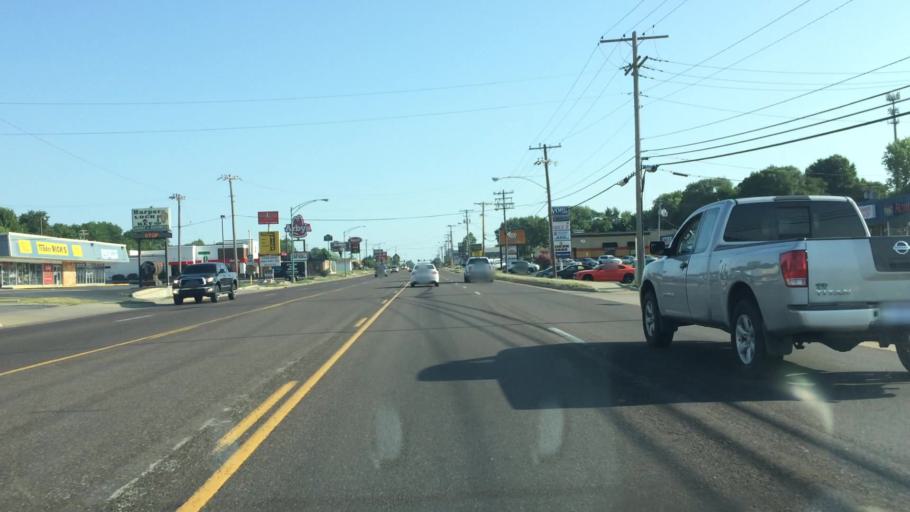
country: US
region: Missouri
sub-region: Greene County
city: Springfield
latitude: 37.1729
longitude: -93.2953
